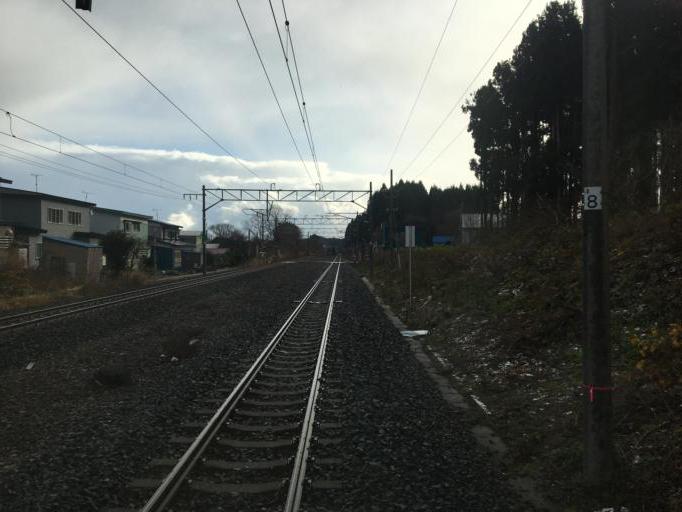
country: JP
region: Aomori
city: Aomori Shi
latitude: 40.9207
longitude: 141.0267
